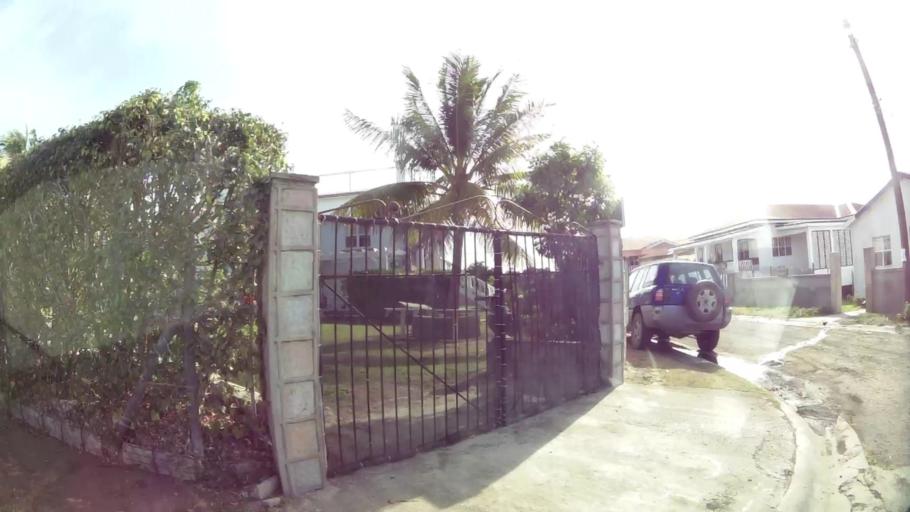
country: KN
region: Saint George Basseterre
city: Basseterre
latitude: 17.2920
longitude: -62.7395
